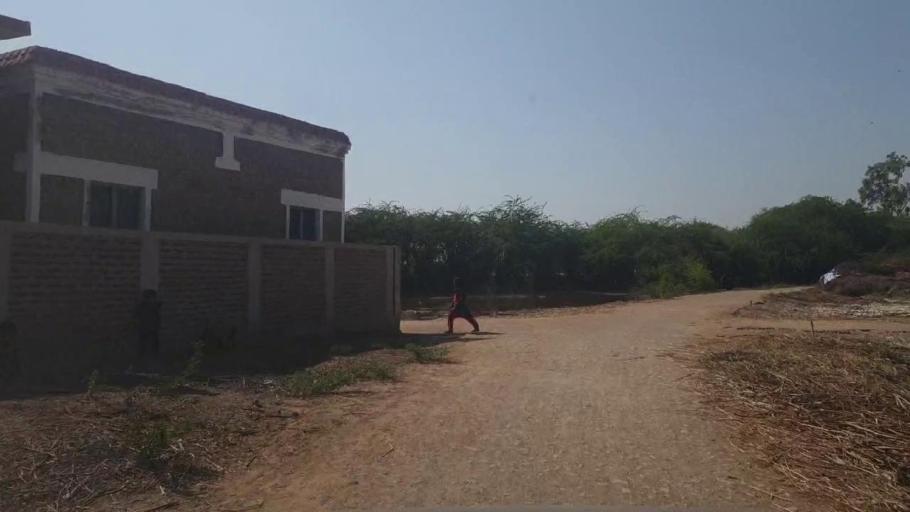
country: PK
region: Sindh
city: Badin
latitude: 24.6275
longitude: 68.9100
